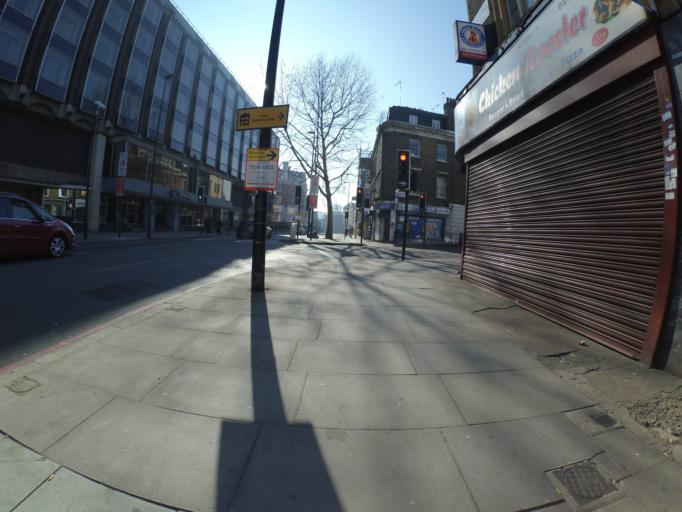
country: GB
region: England
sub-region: Greater London
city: Clerkenwell
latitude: 51.5295
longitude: -0.1158
